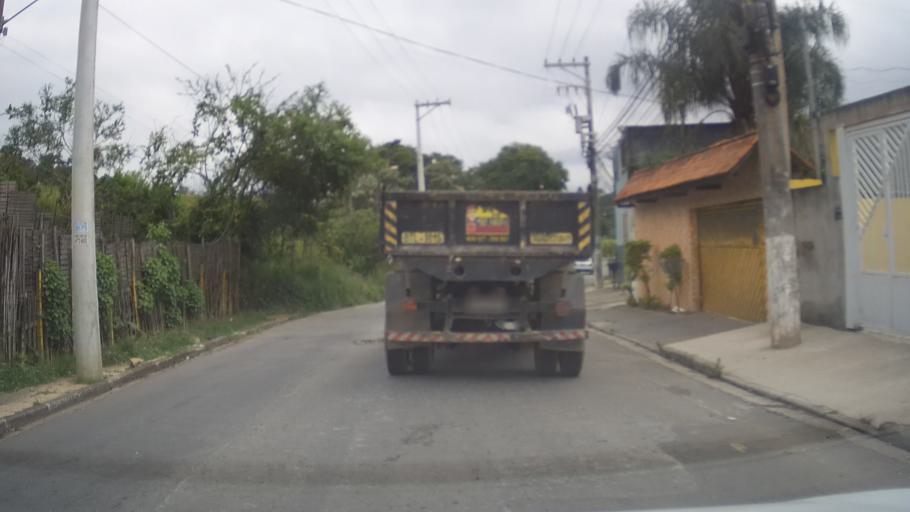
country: BR
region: Sao Paulo
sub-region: Itaquaquecetuba
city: Itaquaquecetuba
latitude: -23.4458
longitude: -46.3779
